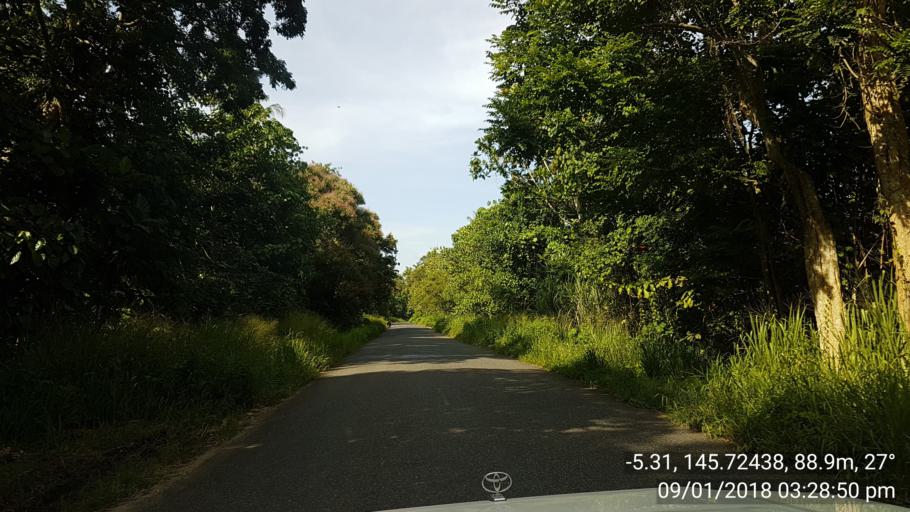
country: PG
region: Madang
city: Madang
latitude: -5.3100
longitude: 145.7244
